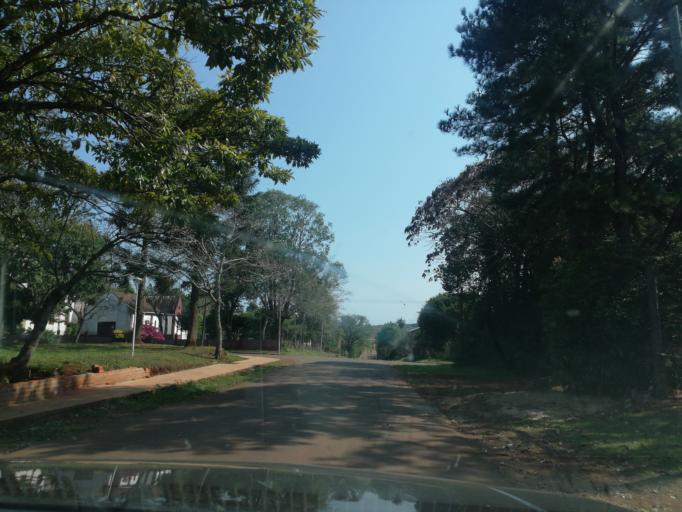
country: AR
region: Misiones
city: Bonpland
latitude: -27.4850
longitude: -55.4796
